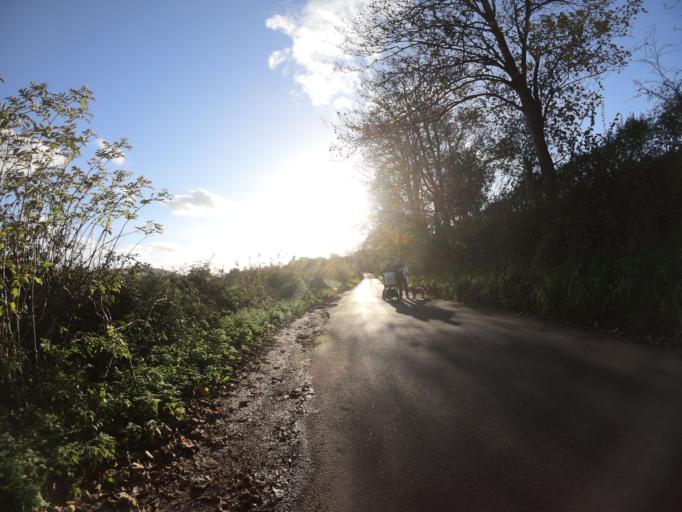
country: GB
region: England
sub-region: Kent
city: Eynsford
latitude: 51.3668
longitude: 0.1985
